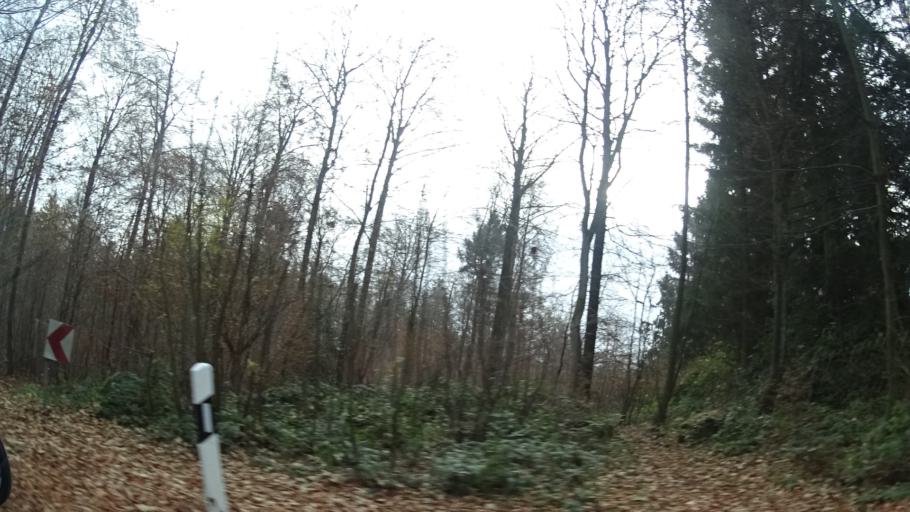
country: DE
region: Baden-Wuerttemberg
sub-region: Karlsruhe Region
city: Gaiberg
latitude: 49.3899
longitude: 8.7391
